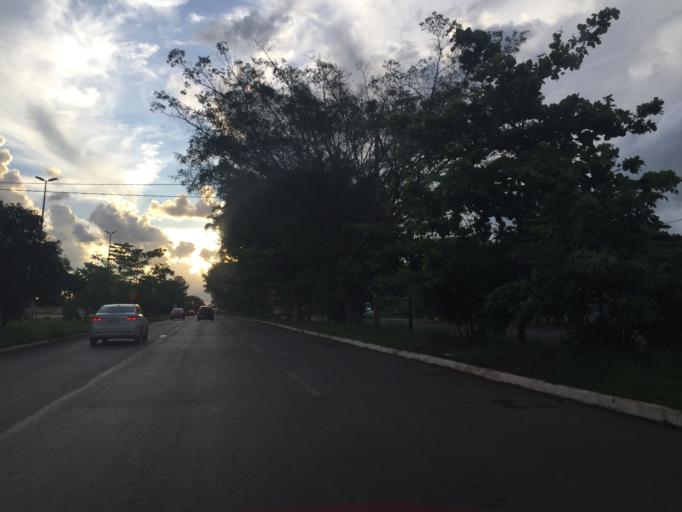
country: BR
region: Federal District
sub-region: Brasilia
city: Brasilia
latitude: -15.7927
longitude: -47.9856
